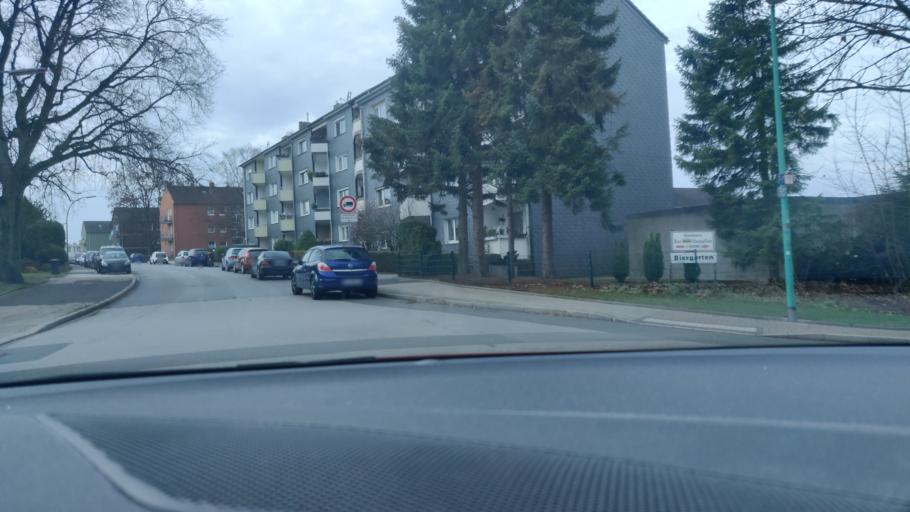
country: DE
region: North Rhine-Westphalia
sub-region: Regierungsbezirk Dusseldorf
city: Velbert
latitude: 51.3345
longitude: 7.0210
